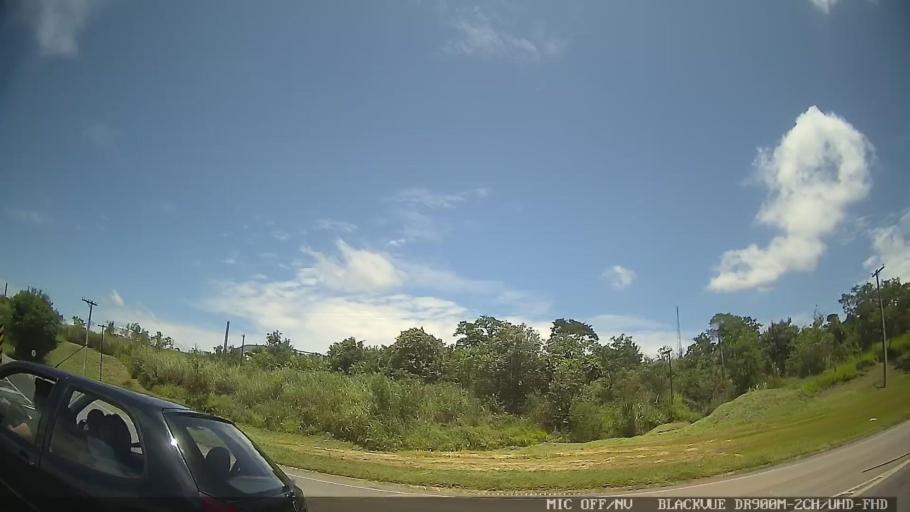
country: BR
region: Sao Paulo
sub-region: Laranjal Paulista
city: Laranjal Paulista
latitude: -23.0631
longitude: -47.8222
